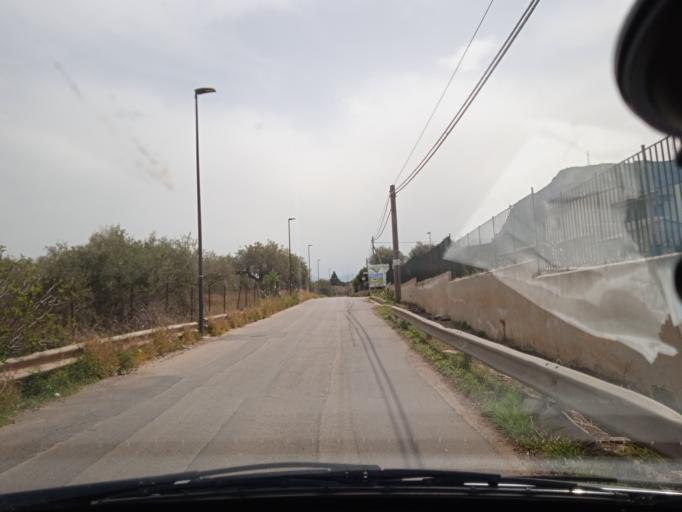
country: IT
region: Sicily
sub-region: Palermo
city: Torre Colonna-Sperone
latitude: 38.0283
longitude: 13.5722
